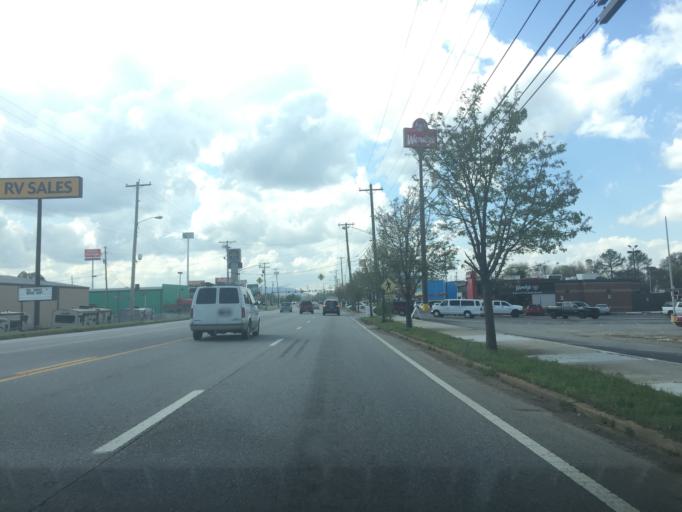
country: US
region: Georgia
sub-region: Catoosa County
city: Indian Springs
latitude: 34.9895
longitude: -85.1962
